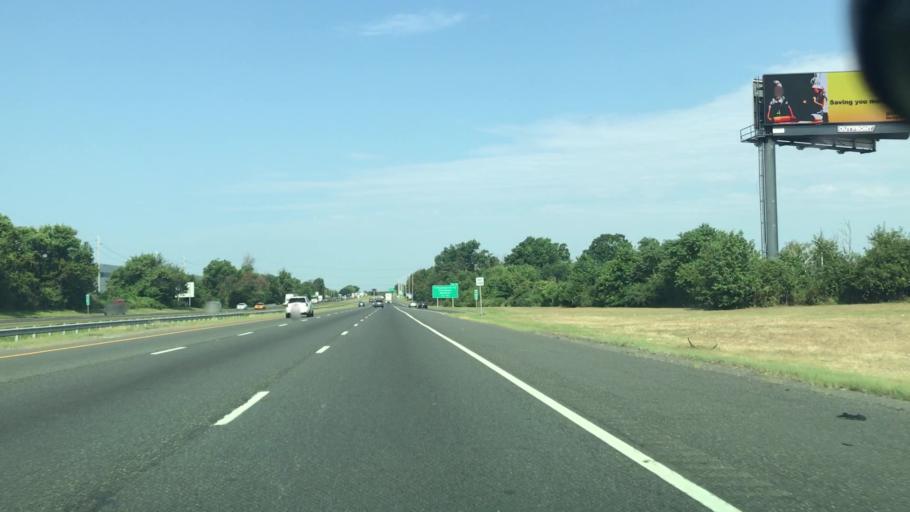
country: US
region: New Jersey
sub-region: Middlesex County
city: Society Hill
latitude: 40.5558
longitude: -74.4479
